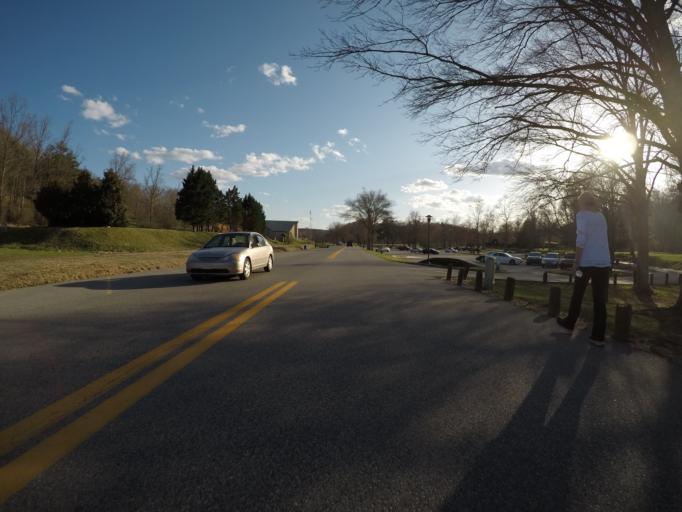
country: US
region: West Virginia
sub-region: Kanawha County
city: Charleston
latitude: 38.3970
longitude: -81.5812
